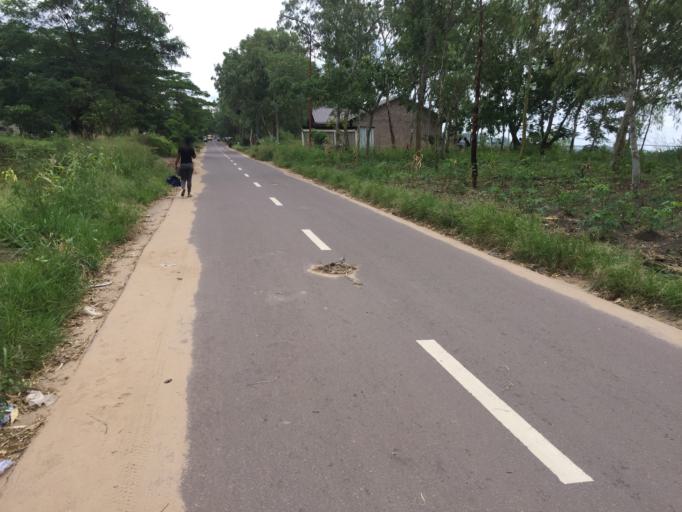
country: CD
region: Kinshasa
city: Kinshasa
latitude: -4.4159
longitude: 15.3054
